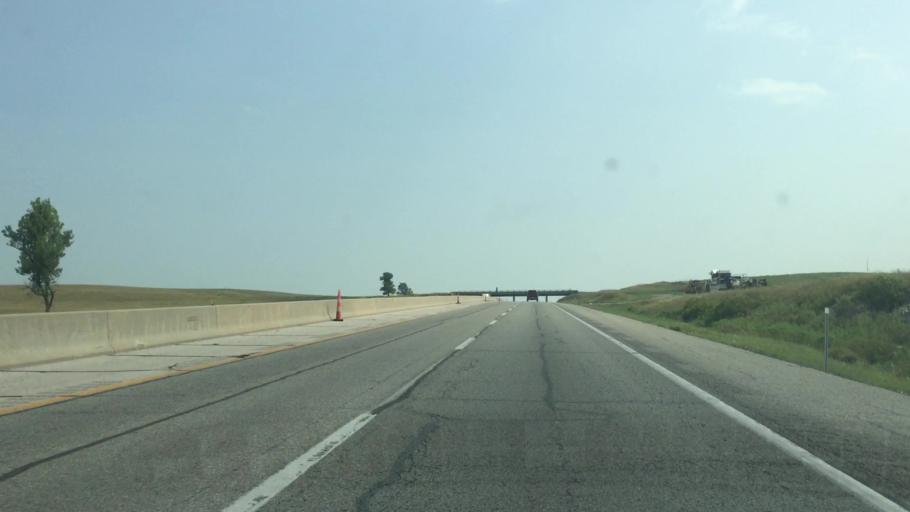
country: US
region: Kansas
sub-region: Chase County
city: Cottonwood Falls
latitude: 38.1587
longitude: -96.4867
